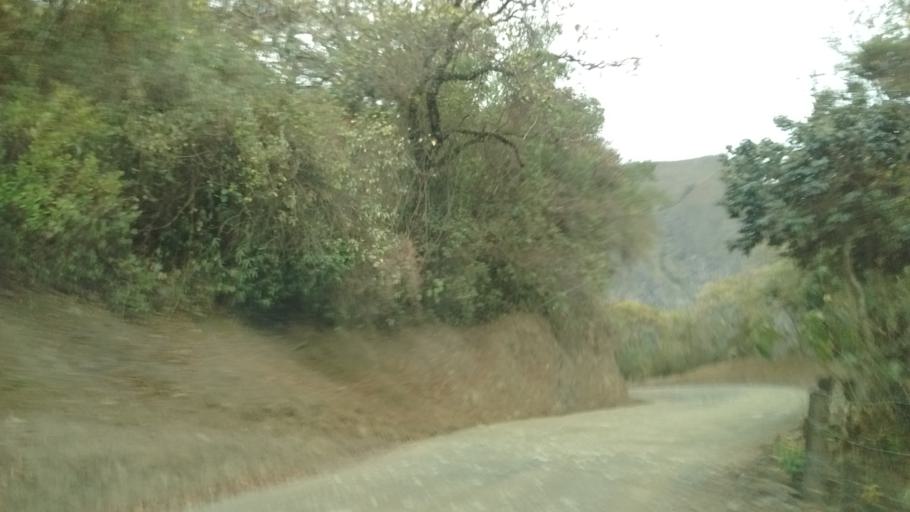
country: CO
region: Cauca
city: Almaguer
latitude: 1.8570
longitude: -76.9391
